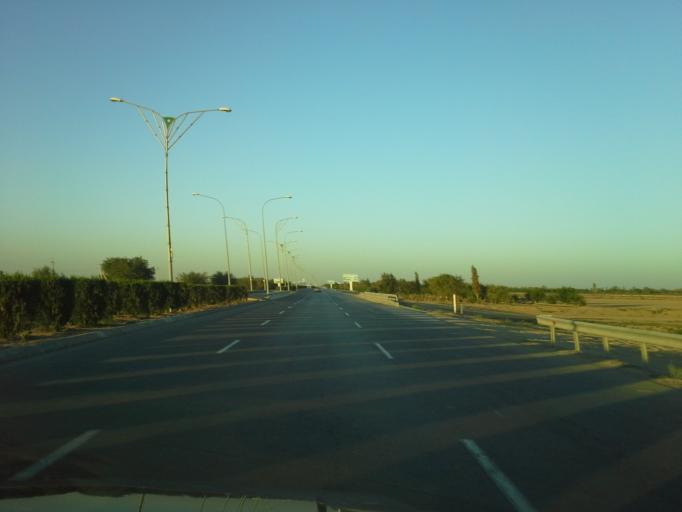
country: TM
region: Dasoguz
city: Dasoguz
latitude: 41.7962
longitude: 59.8910
